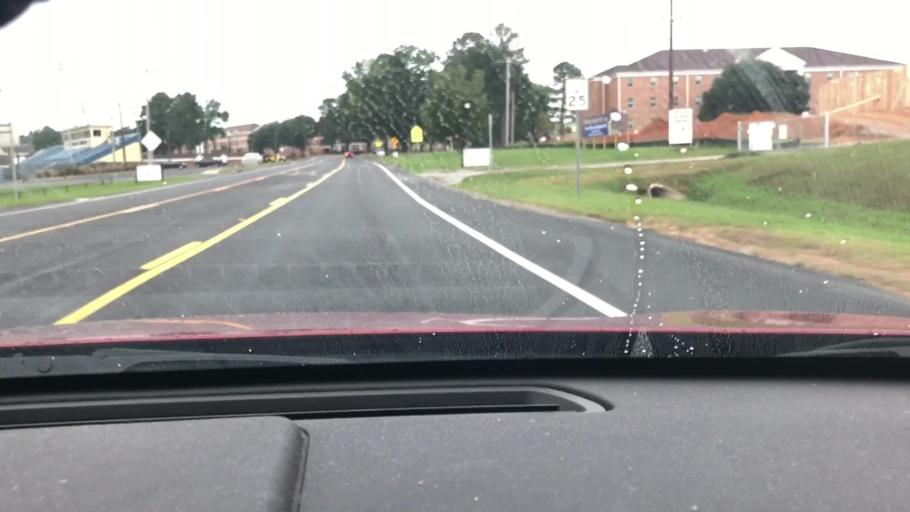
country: US
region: Arkansas
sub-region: Columbia County
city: Magnolia
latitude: 33.2963
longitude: -93.2373
